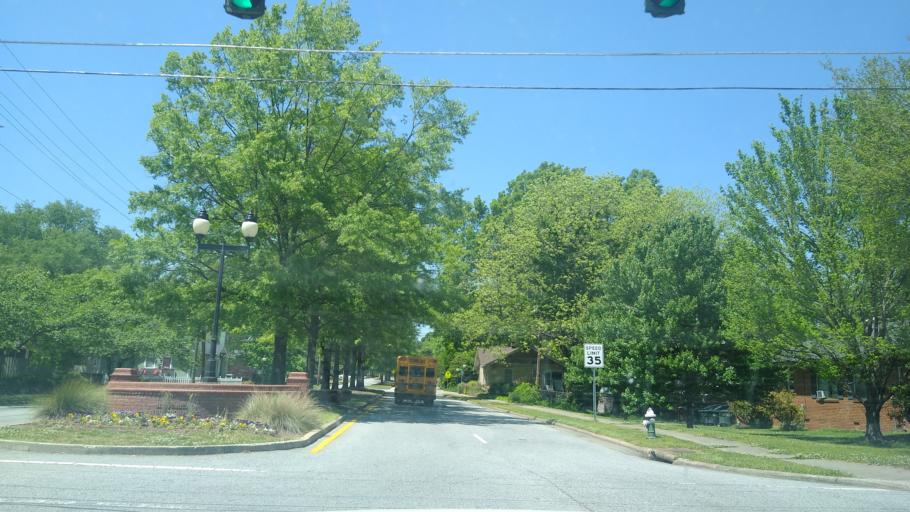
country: US
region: North Carolina
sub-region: Guilford County
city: Greensboro
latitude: 36.0808
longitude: -79.7802
